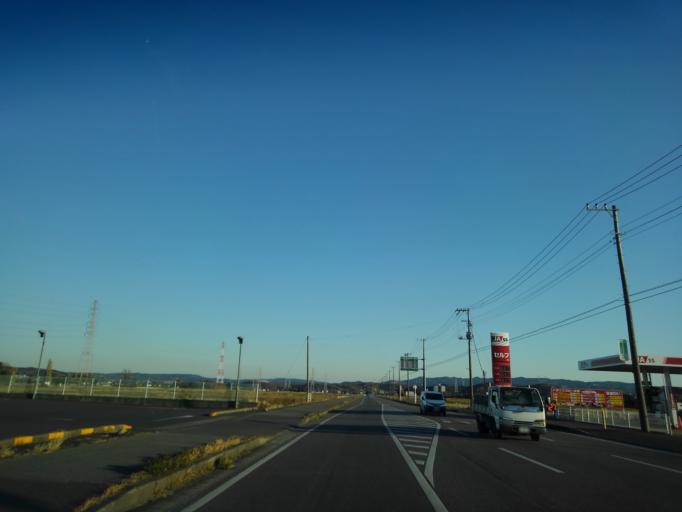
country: JP
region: Chiba
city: Kimitsu
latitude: 35.3195
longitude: 139.9053
